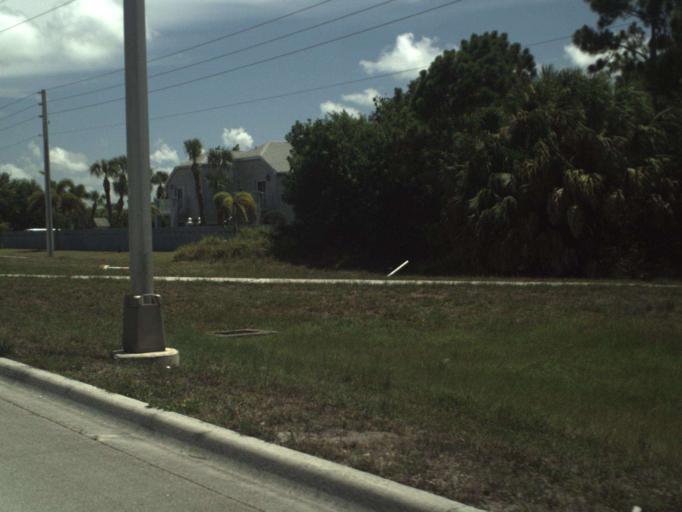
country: US
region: Florida
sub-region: Saint Lucie County
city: Port Saint Lucie
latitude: 27.2938
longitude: -80.3017
